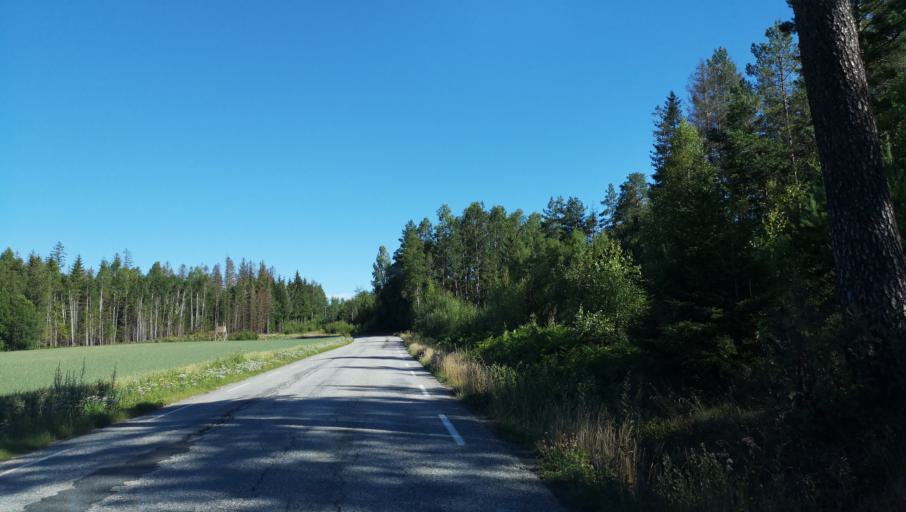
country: NO
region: Ostfold
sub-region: Hobol
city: Knappstad
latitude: 59.6407
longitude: 11.0164
